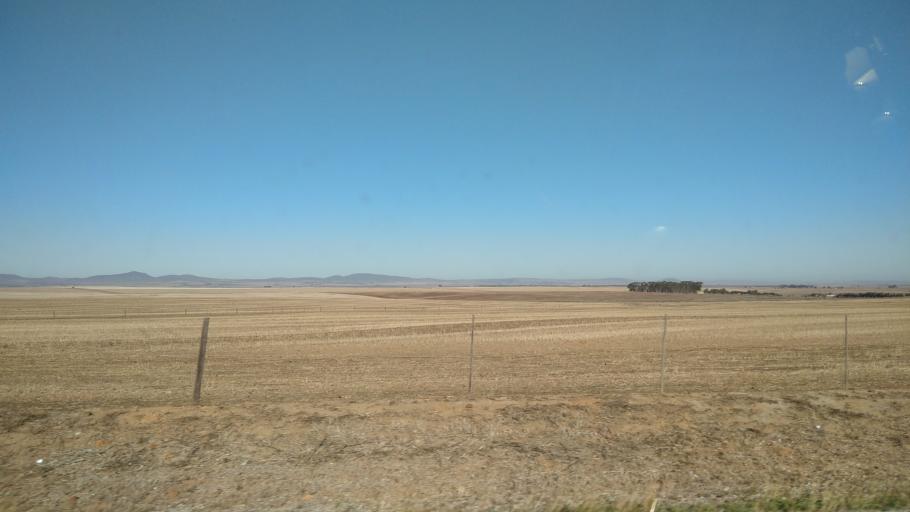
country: ZA
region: Western Cape
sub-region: West Coast District Municipality
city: Malmesbury
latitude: -33.3332
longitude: 18.6324
